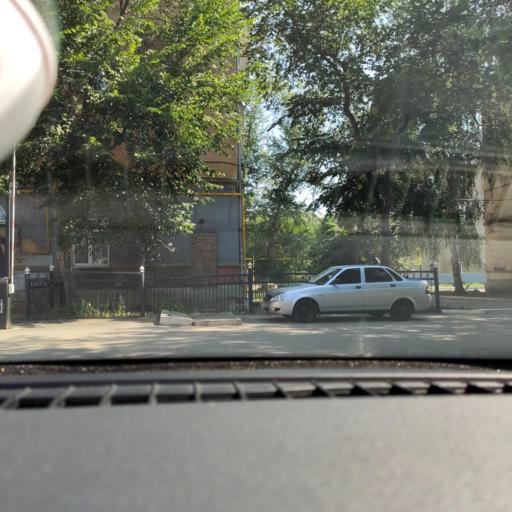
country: RU
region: Samara
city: Samara
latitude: 53.1145
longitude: 50.0775
